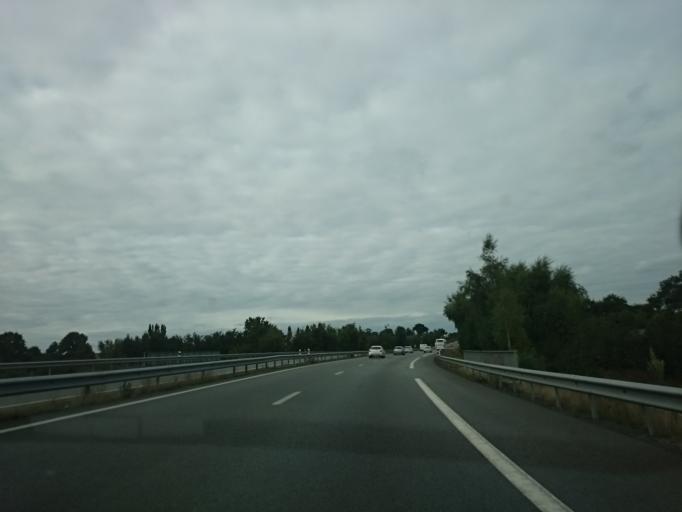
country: FR
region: Brittany
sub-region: Departement d'Ille-et-Vilaine
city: La Dominelais
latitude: 47.7818
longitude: -1.6992
